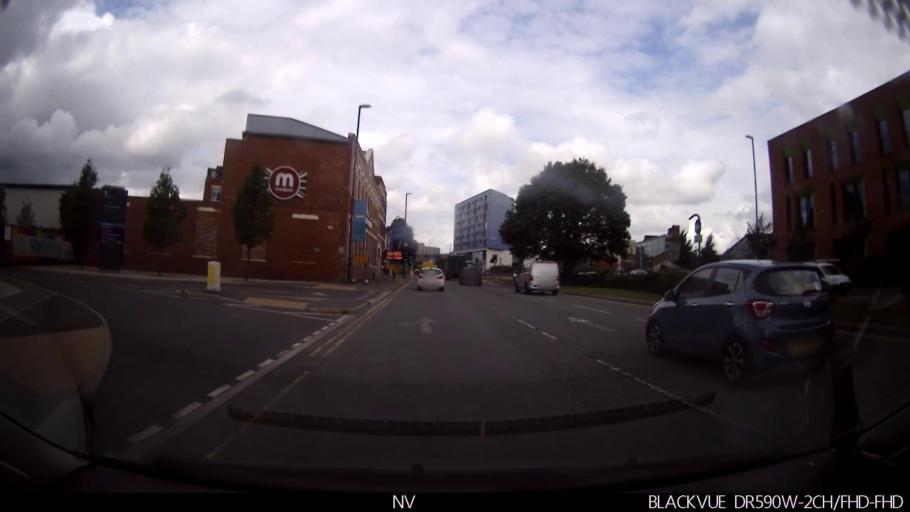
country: GB
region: England
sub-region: City and Borough of Leeds
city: Leeds
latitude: 53.7895
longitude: -1.5373
